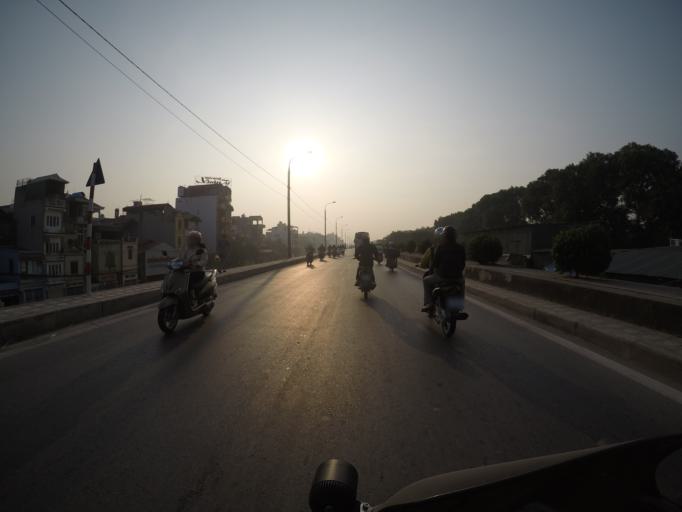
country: VN
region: Ha Noi
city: Hoan Kiem
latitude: 21.0364
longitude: 105.8710
